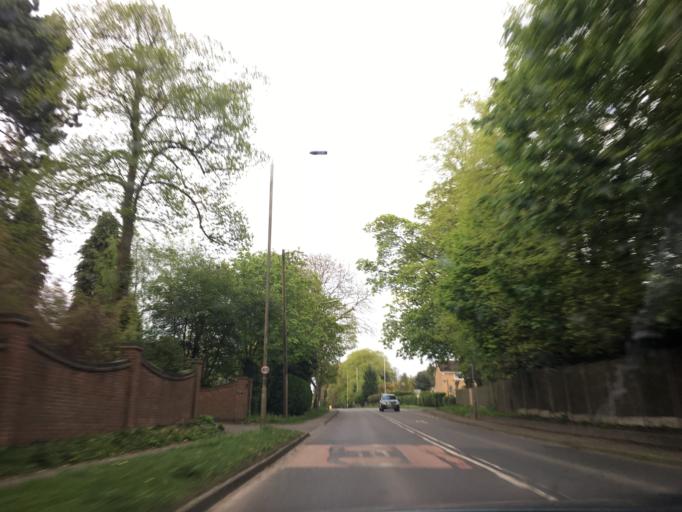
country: GB
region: England
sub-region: Leicestershire
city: Houghton on the Hill
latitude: 52.6301
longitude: -1.0376
